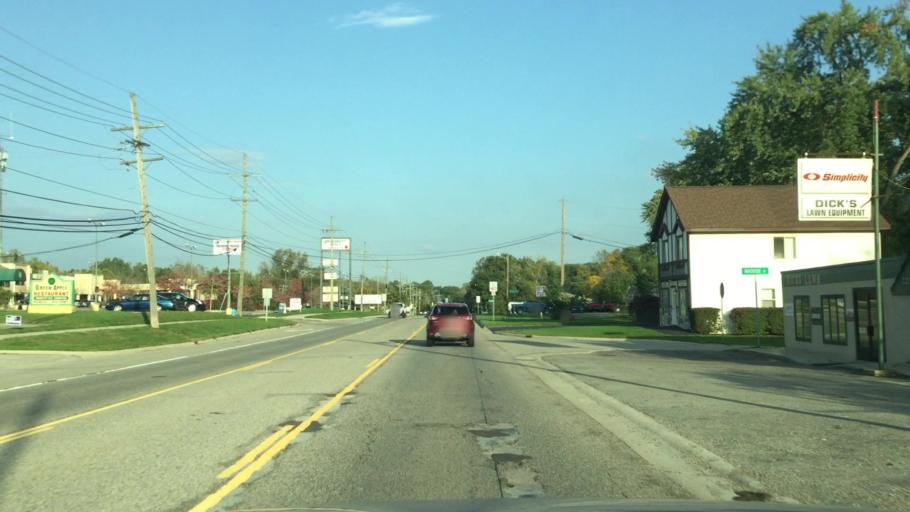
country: US
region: Michigan
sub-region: Oakland County
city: West Bloomfield Township
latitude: 42.6153
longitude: -83.4277
